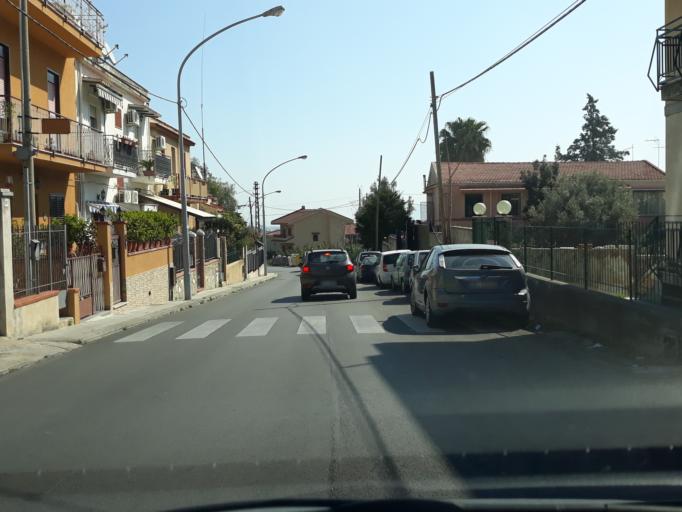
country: IT
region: Sicily
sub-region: Palermo
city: Piano dei Geli
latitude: 38.1173
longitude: 13.2938
